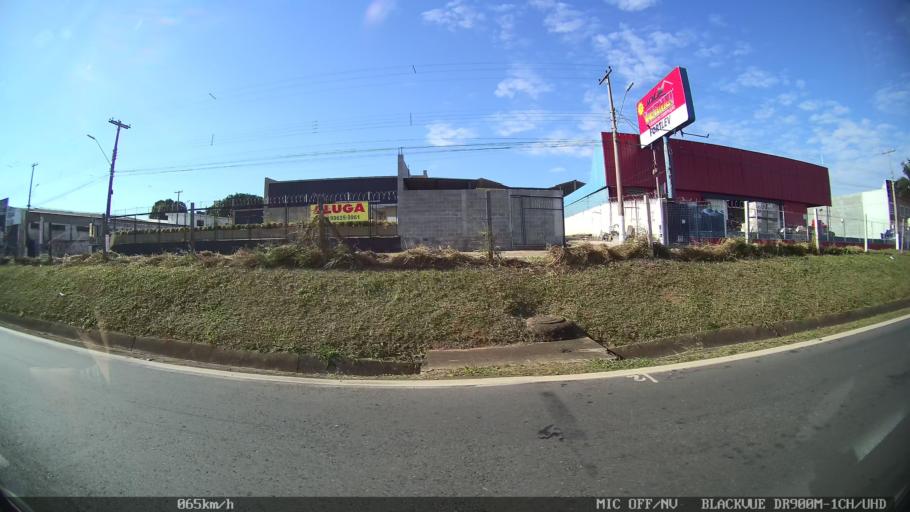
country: BR
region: Sao Paulo
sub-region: Nova Odessa
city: Nova Odessa
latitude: -22.7507
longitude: -47.2604
